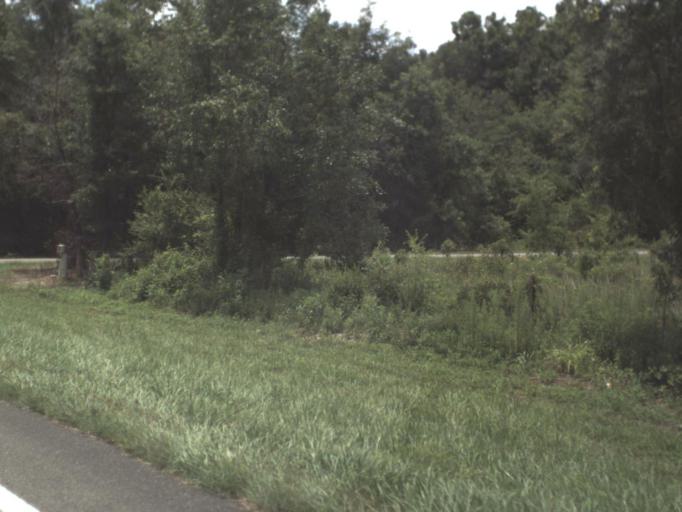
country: US
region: Florida
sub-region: Levy County
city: Williston
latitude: 29.4567
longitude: -82.4747
